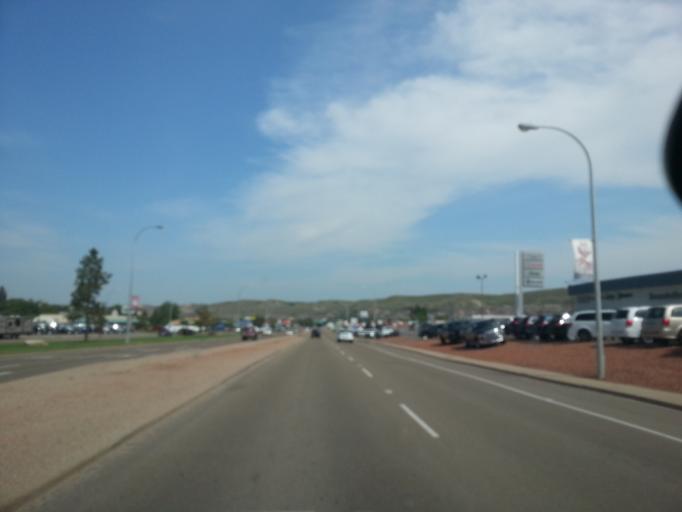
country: CA
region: Alberta
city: Three Hills
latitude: 51.4526
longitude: -112.7005
